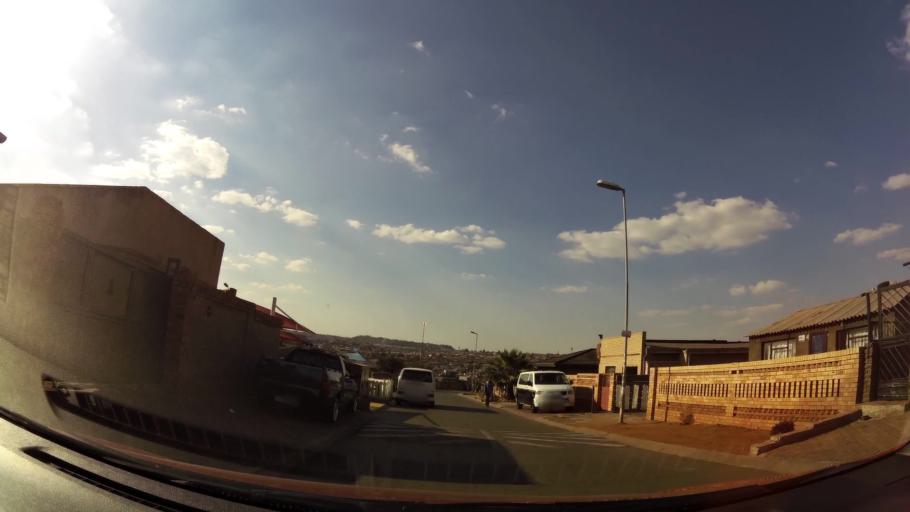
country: ZA
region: Gauteng
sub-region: City of Johannesburg Metropolitan Municipality
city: Soweto
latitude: -26.2263
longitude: 27.8775
